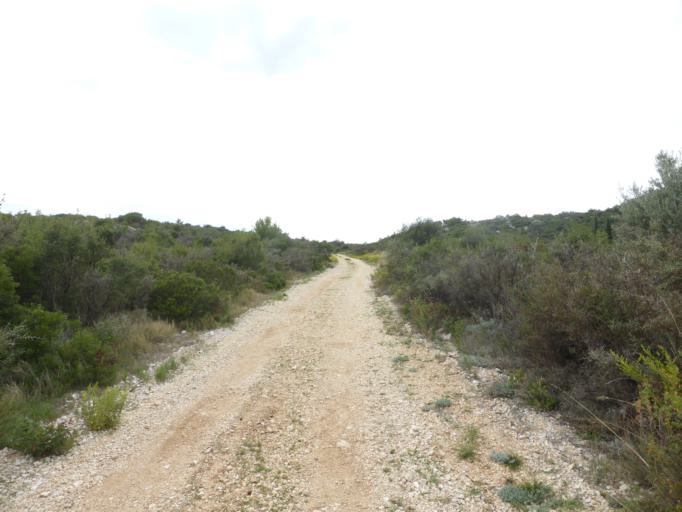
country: HR
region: Dubrovacko-Neretvanska
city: Podgora
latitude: 42.7776
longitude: 17.8689
